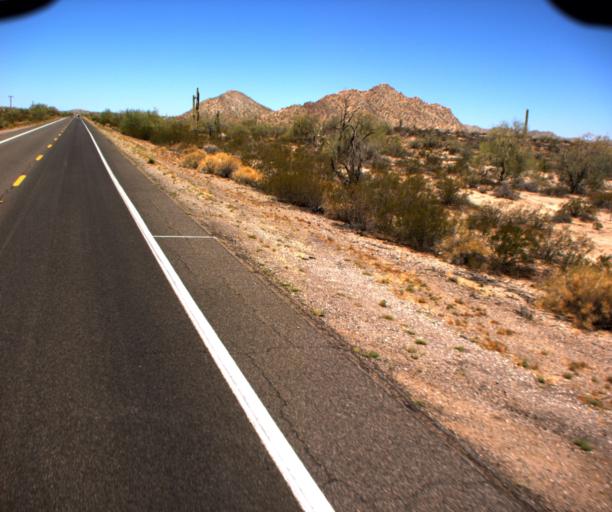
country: US
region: Arizona
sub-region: Pinal County
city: Maricopa
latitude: 32.8414
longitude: -112.1097
